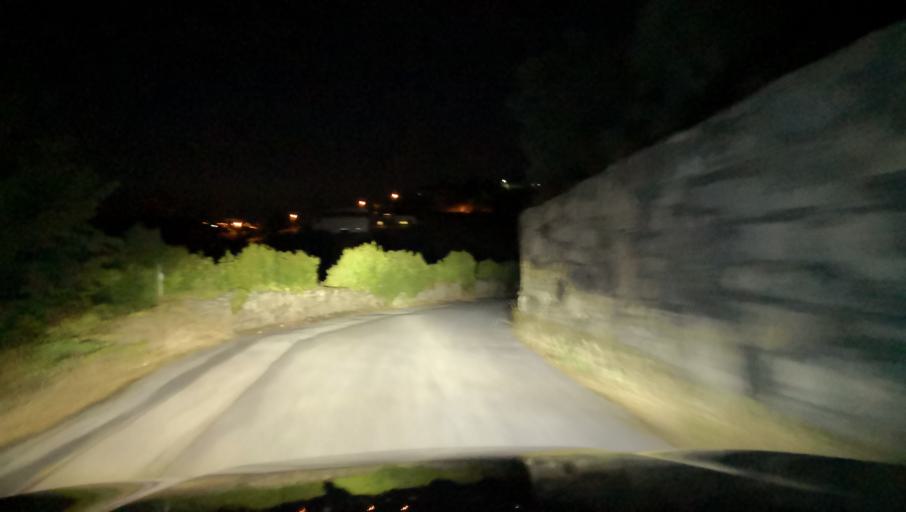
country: PT
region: Vila Real
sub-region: Peso da Regua
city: Peso da Regua
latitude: 41.1714
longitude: -7.7296
